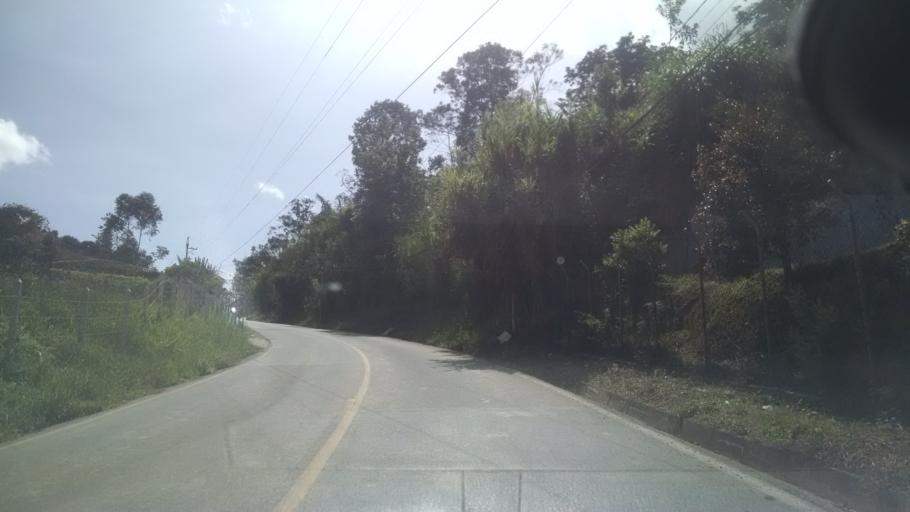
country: CO
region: Antioquia
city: San Vicente
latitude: 6.2260
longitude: -75.2543
